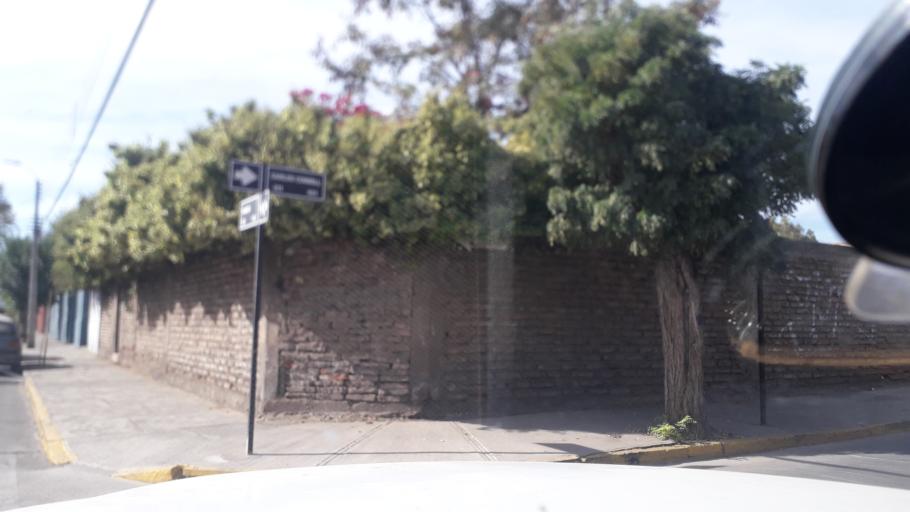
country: CL
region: Valparaiso
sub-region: Provincia de San Felipe
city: San Felipe
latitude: -32.7472
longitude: -70.7274
